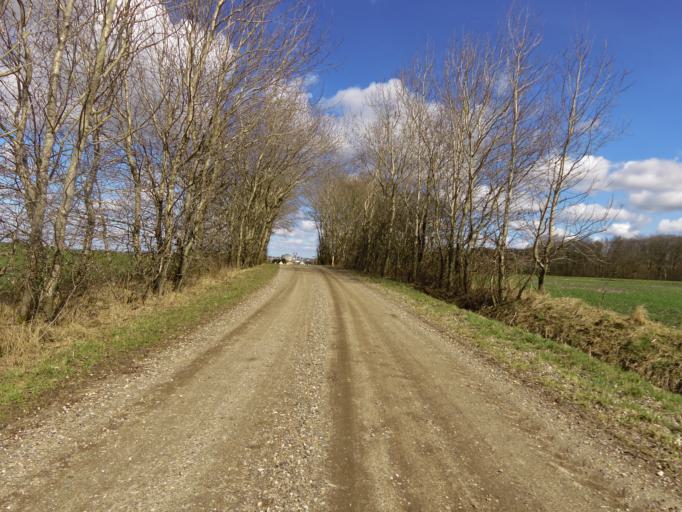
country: DK
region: South Denmark
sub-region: Tonder Kommune
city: Toftlund
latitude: 55.1577
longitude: 9.0480
